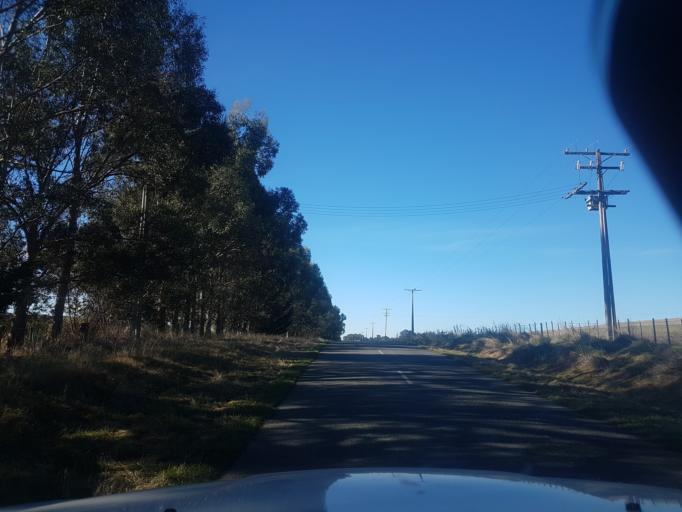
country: NZ
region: Canterbury
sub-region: Timaru District
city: Pleasant Point
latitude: -44.2899
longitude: 171.0690
